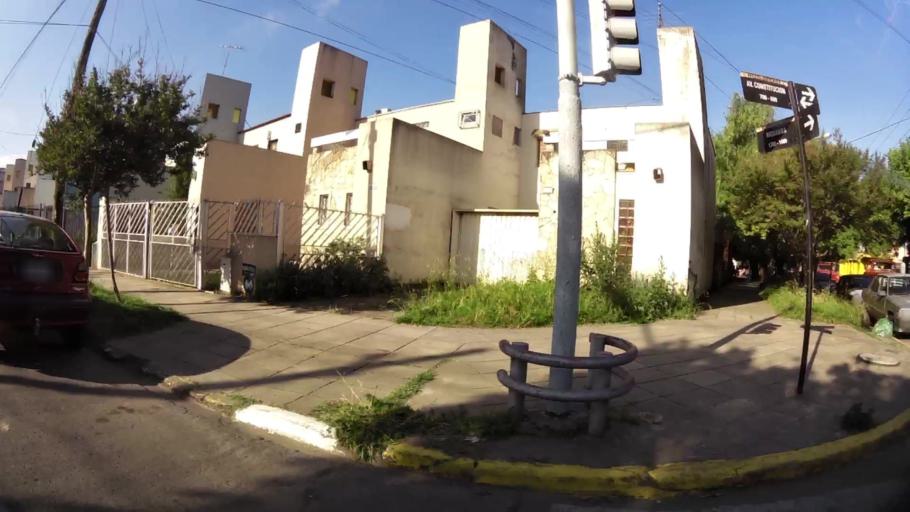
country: AR
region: Buenos Aires
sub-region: Partido de Merlo
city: Merlo
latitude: -34.6705
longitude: -58.7353
